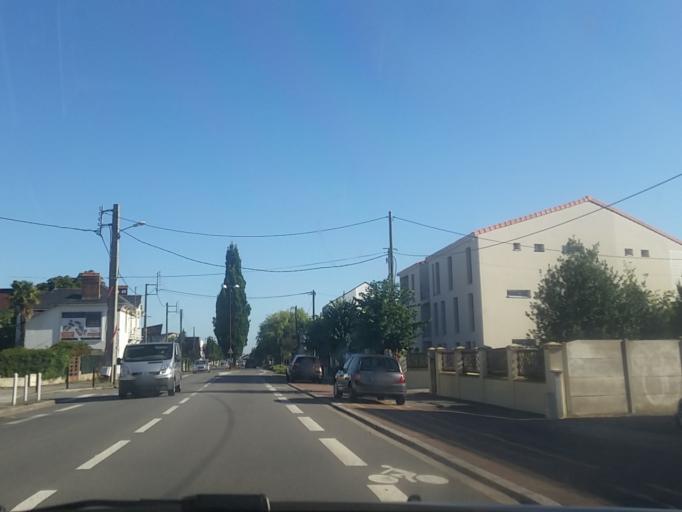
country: FR
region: Pays de la Loire
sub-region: Departement de la Loire-Atlantique
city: Reze
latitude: 47.1719
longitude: -1.5433
